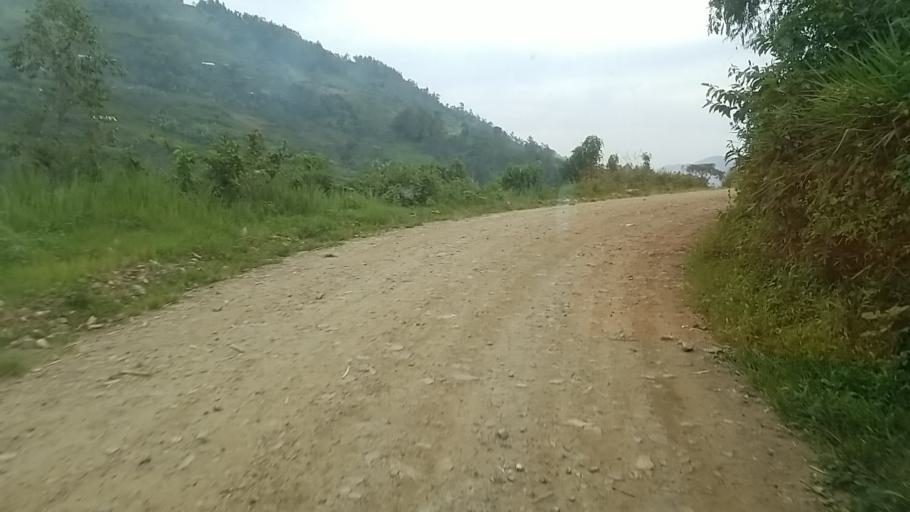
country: CD
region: Nord Kivu
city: Sake
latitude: -1.9534
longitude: 28.9259
